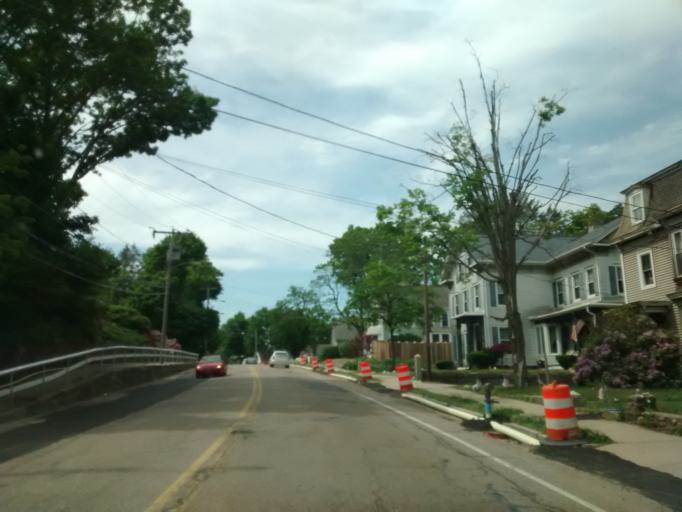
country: US
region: Massachusetts
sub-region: Worcester County
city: Uxbridge
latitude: 42.0782
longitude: -71.6309
